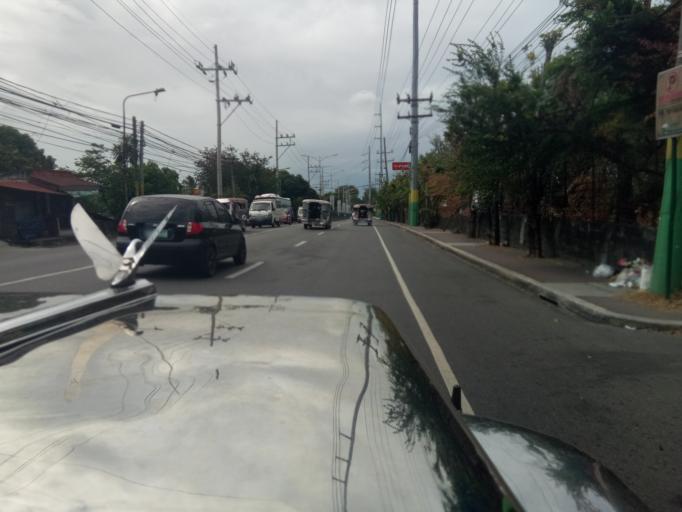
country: PH
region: Calabarzon
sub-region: Province of Cavite
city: Dasmarinas
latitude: 14.3054
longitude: 120.9534
